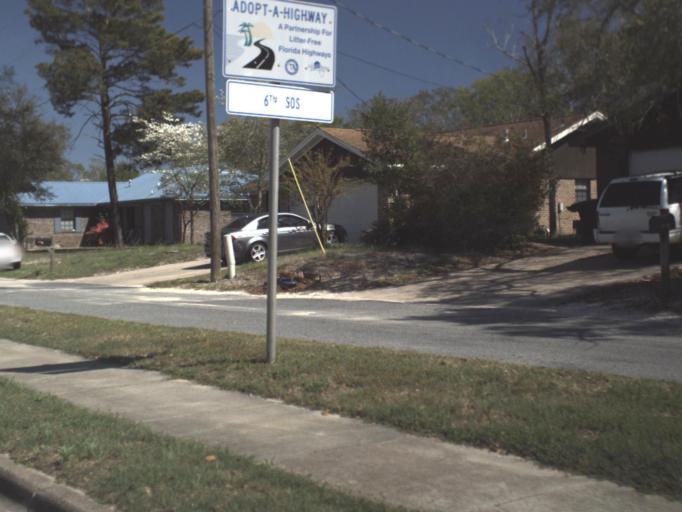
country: US
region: Florida
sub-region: Okaloosa County
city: Ocean City
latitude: 30.4272
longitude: -86.6300
